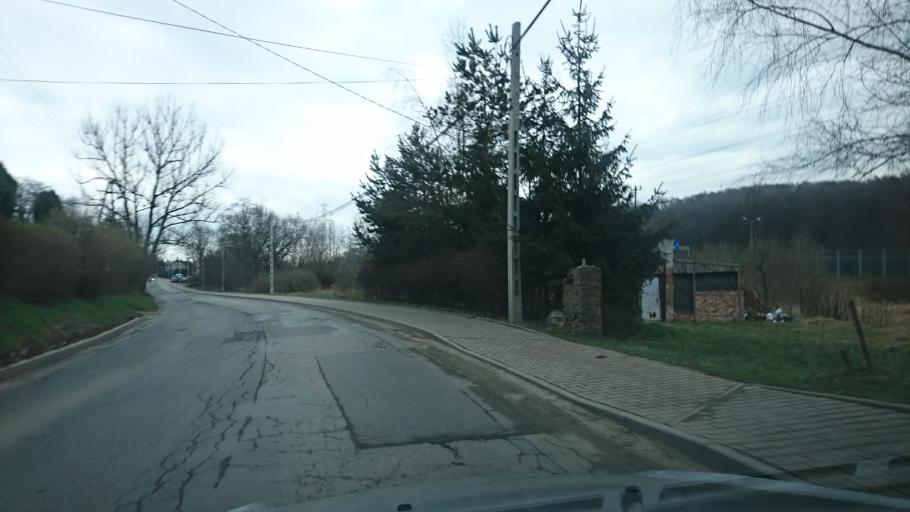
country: PL
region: Lesser Poland Voivodeship
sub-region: Powiat wielicki
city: Wieliczka
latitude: 50.0037
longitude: 20.0076
